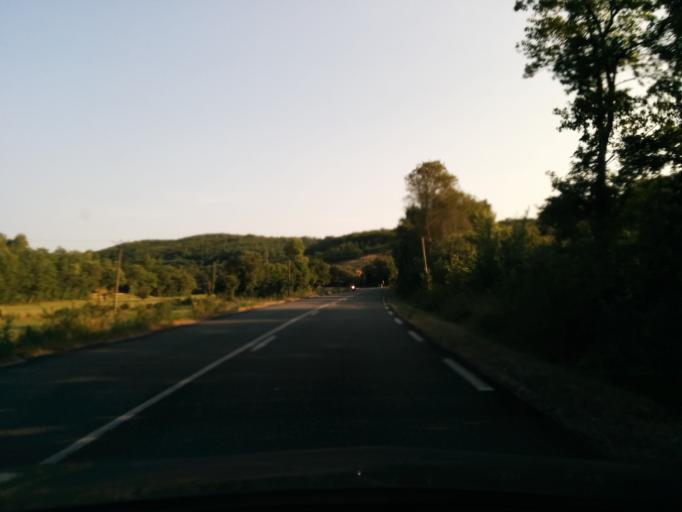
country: FR
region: Midi-Pyrenees
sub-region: Departement du Lot
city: Le Vigan
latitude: 44.7036
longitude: 1.4803
